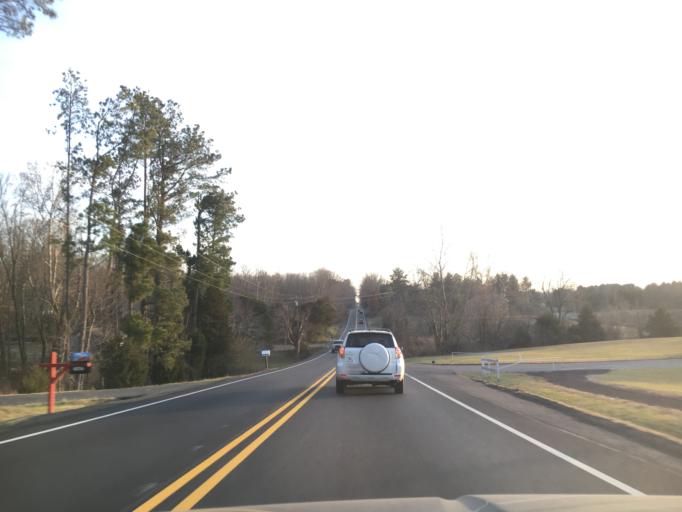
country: US
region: Virginia
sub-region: Orange County
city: Orange
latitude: 38.2987
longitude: -77.9563
